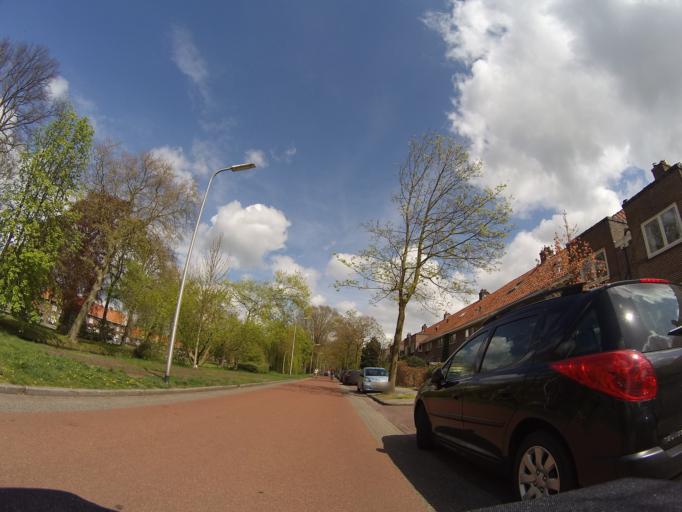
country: NL
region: Overijssel
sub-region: Gemeente Zwolle
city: Zwolle
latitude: 52.5150
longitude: 6.1097
